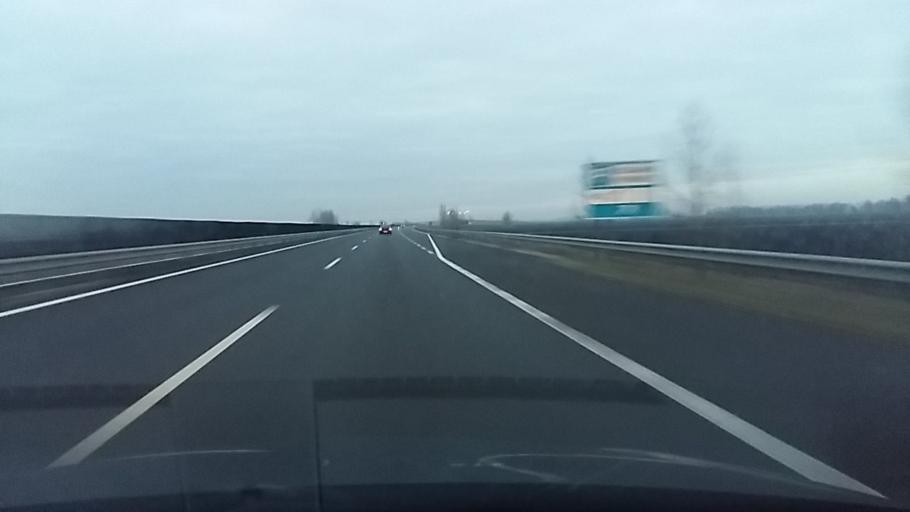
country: HU
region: Hajdu-Bihar
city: Hajduboszormeny
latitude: 47.6969
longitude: 21.4395
